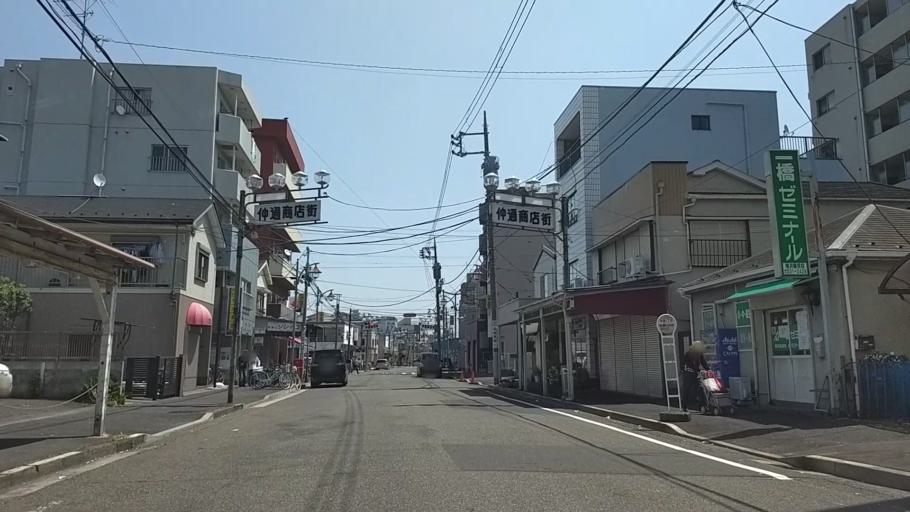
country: JP
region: Kanagawa
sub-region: Kawasaki-shi
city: Kawasaki
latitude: 35.5014
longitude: 139.6870
